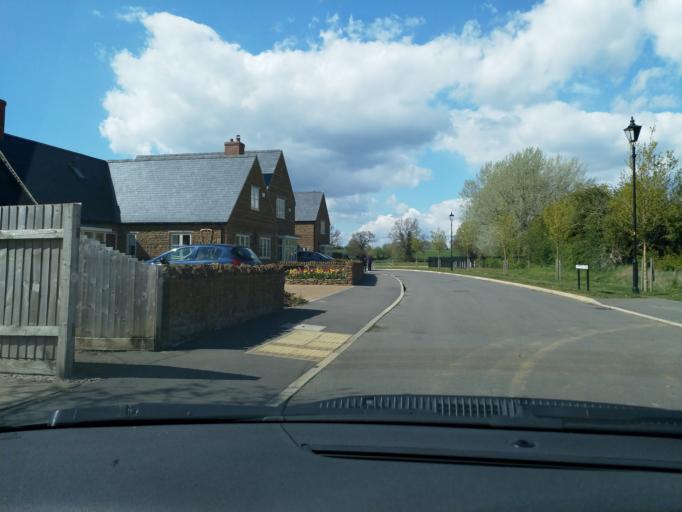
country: GB
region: England
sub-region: Oxfordshire
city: Adderbury
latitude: 52.0257
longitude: -1.2752
